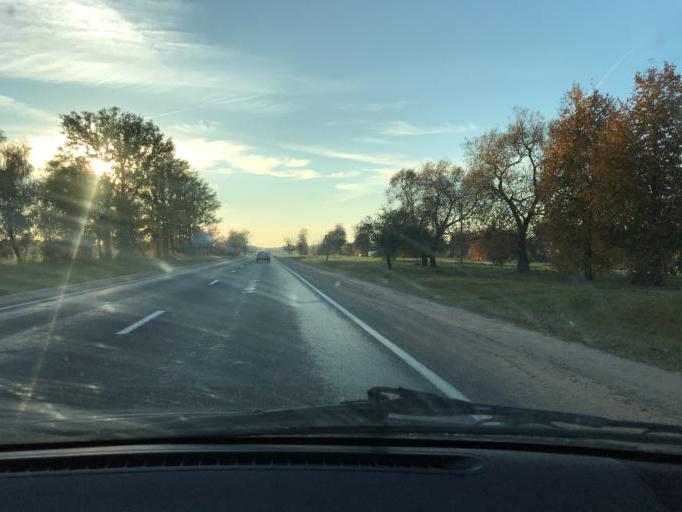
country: BY
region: Brest
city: Horad Kobryn
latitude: 52.2177
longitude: 24.4118
